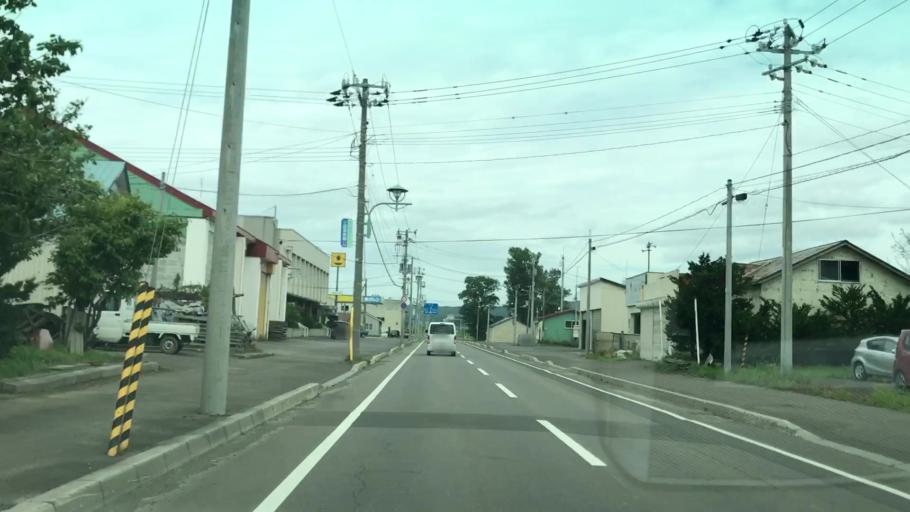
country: JP
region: Hokkaido
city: Iwanai
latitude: 43.0146
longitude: 140.5703
